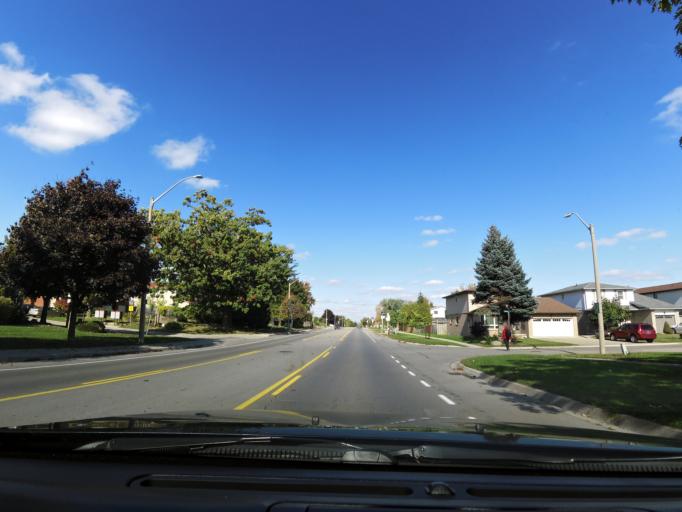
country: CA
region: Ontario
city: Ancaster
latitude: 43.2214
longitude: -79.9172
